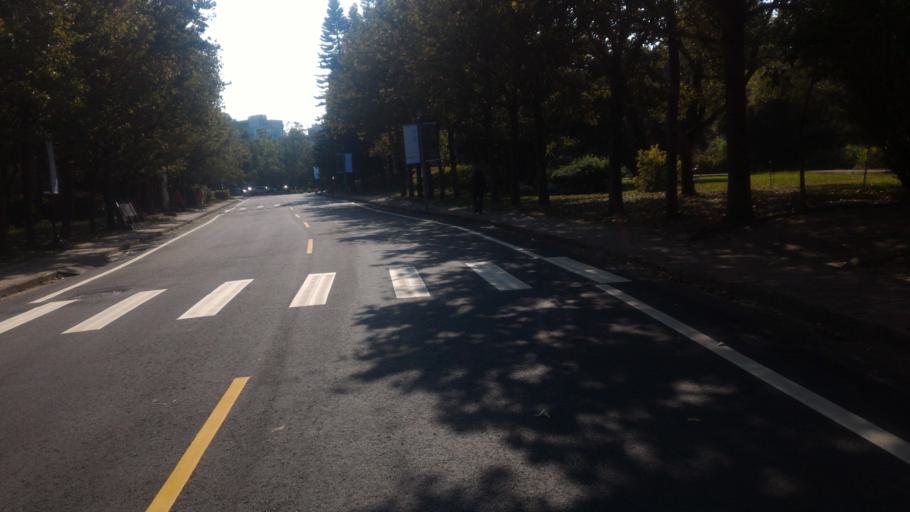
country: TW
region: Taiwan
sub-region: Hsinchu
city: Hsinchu
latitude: 24.7587
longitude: 120.9536
